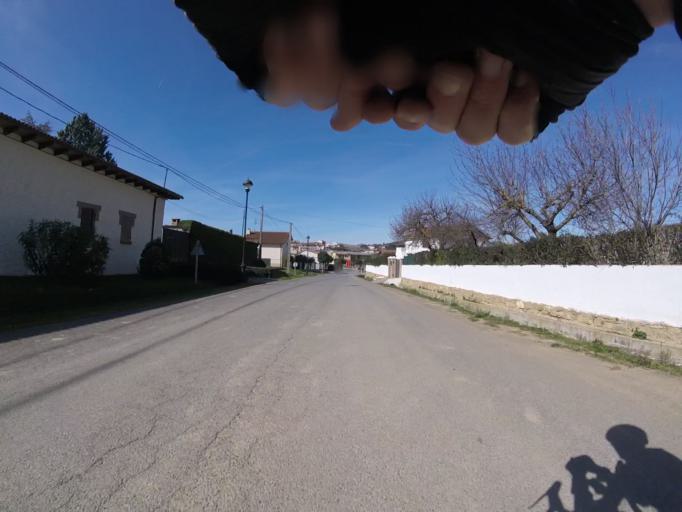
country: ES
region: Navarre
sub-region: Provincia de Navarra
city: Villatuerta
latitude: 42.6586
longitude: -1.9884
